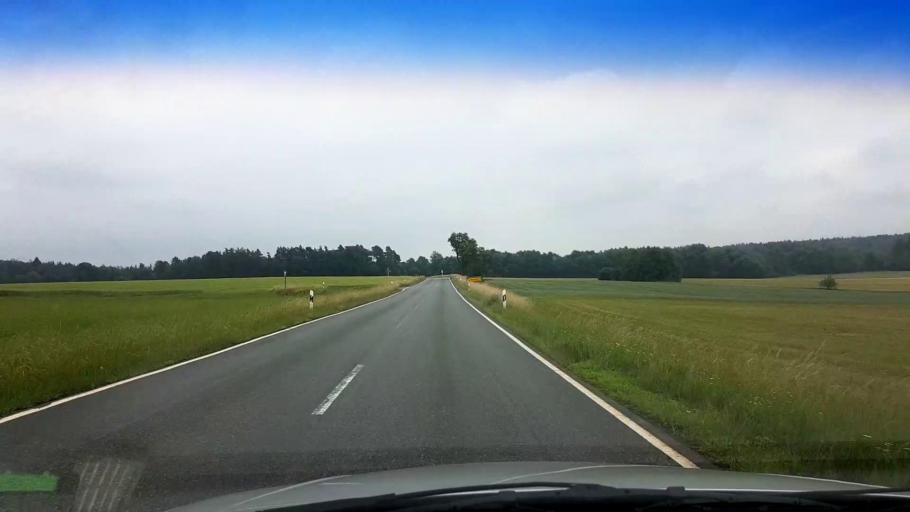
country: DE
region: Bavaria
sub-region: Upper Franconia
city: Weismain
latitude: 50.0865
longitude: 11.2861
